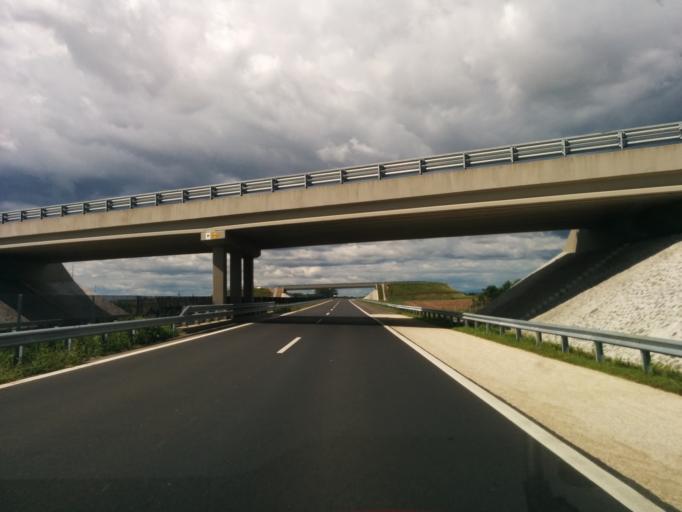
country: HU
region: Vas
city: Vep
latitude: 47.2553
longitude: 16.6973
